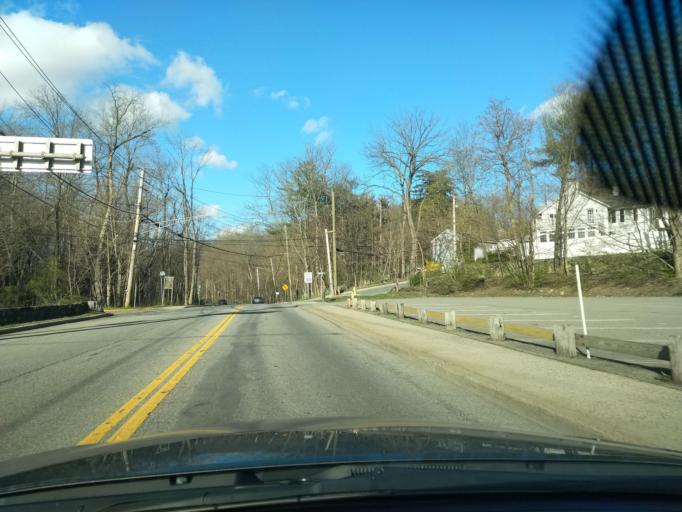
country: US
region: New York
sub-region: Westchester County
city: Mount Kisco
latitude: 41.2077
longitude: -73.7259
